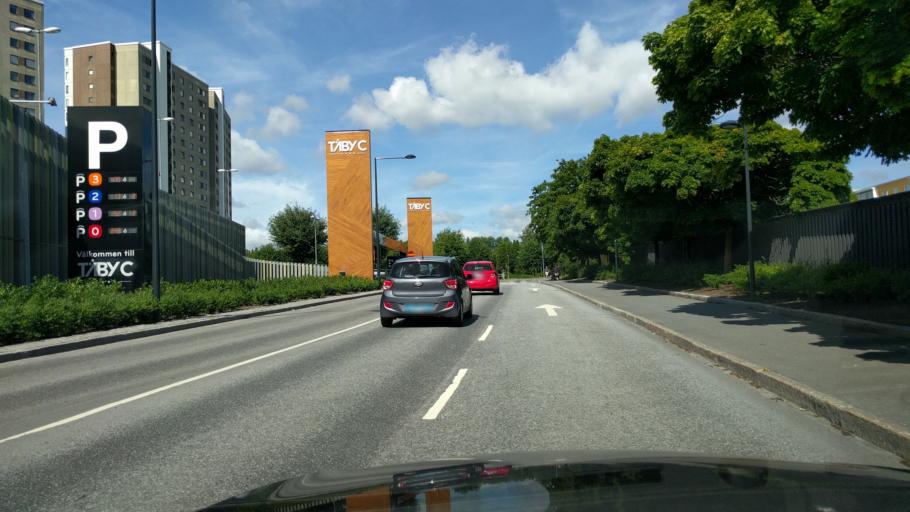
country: SE
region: Stockholm
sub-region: Taby Kommun
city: Taby
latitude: 59.4460
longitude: 18.0744
